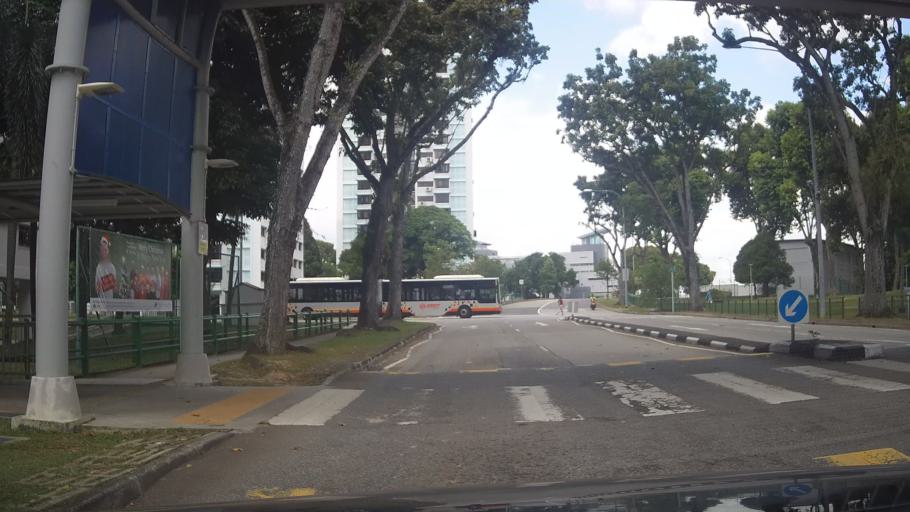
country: MY
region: Johor
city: Johor Bahru
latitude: 1.4457
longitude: 103.7732
